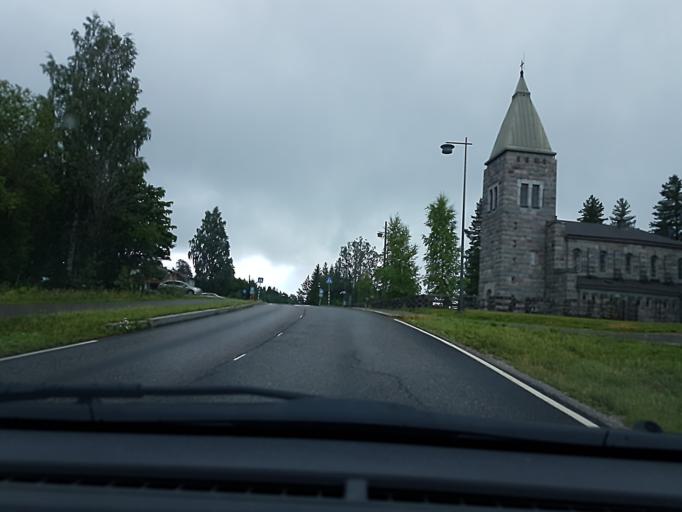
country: FI
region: Uusimaa
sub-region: Helsinki
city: Pornainen
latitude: 60.4748
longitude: 25.3760
